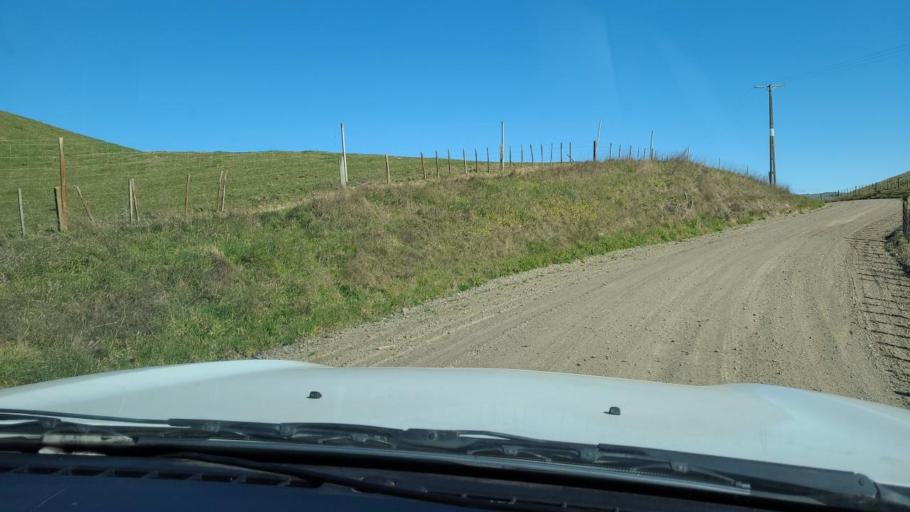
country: NZ
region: Hawke's Bay
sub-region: Napier City
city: Taradale
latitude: -39.4908
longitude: 176.4765
